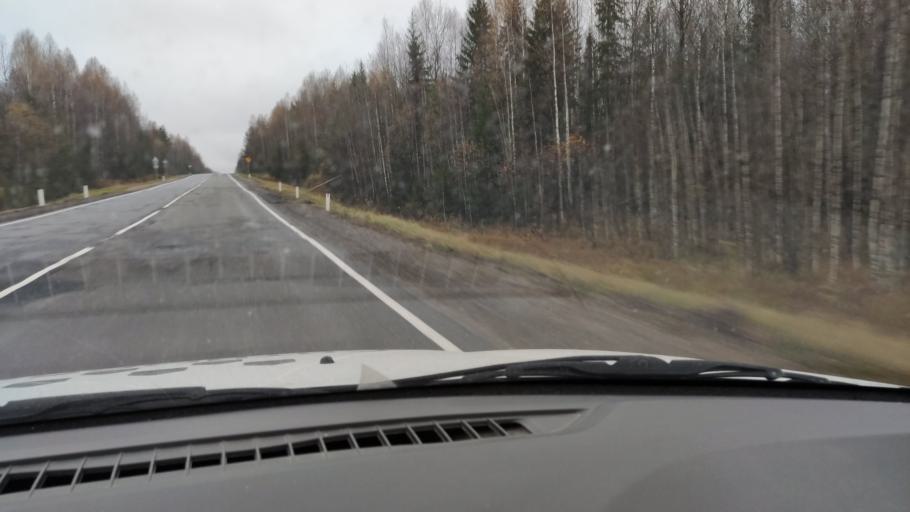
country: RU
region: Kirov
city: Chernaya Kholunitsa
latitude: 58.7730
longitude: 51.9442
